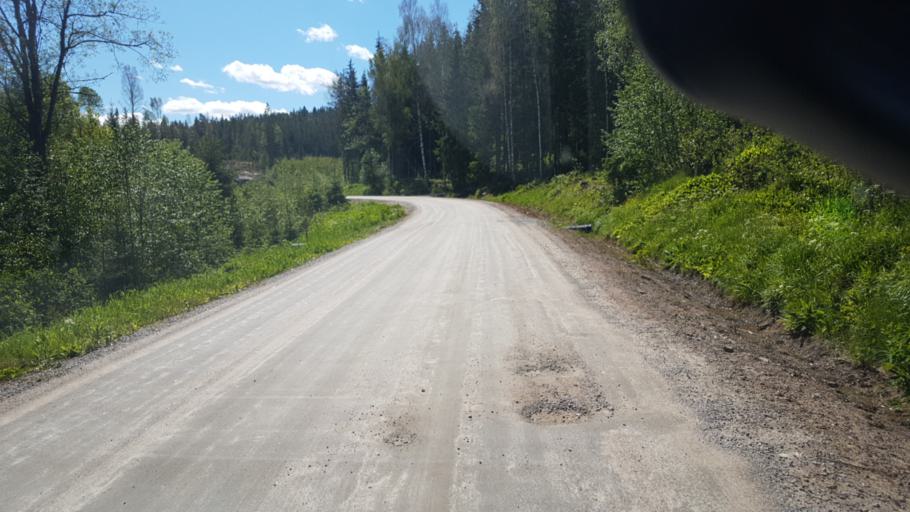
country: SE
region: Vaermland
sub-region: Arvika Kommun
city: Arvika
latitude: 59.6599
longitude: 12.7606
